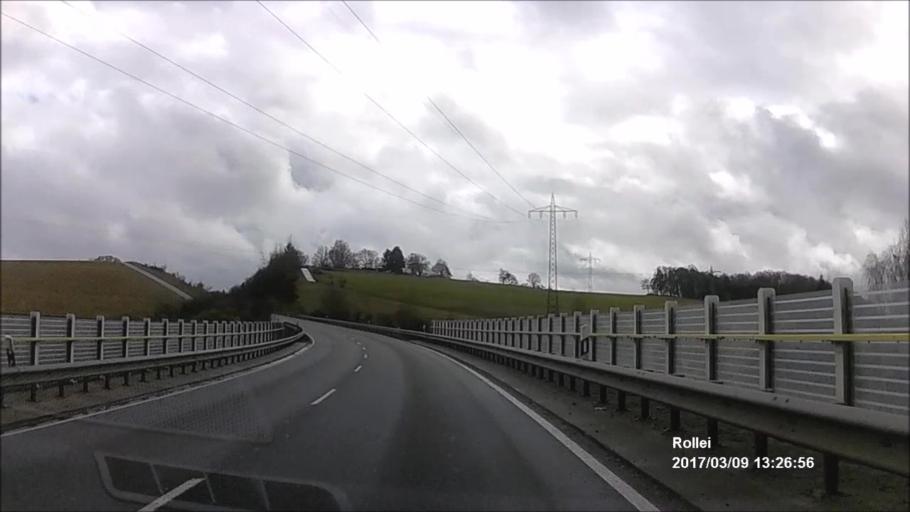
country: DE
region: Rheinland-Pfalz
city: Katzweiler
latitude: 49.4825
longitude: 7.7052
